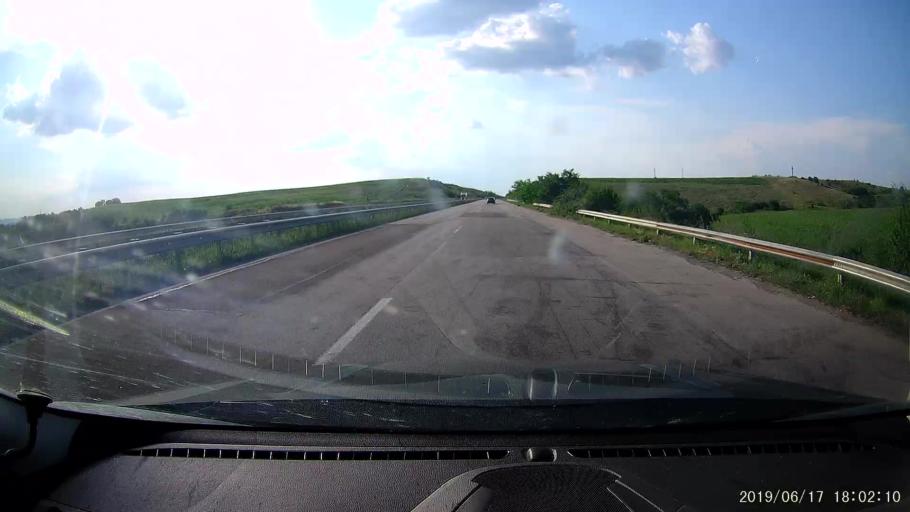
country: BG
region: Khaskovo
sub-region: Obshtina Svilengrad
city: Svilengrad
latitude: 41.7551
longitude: 26.2359
